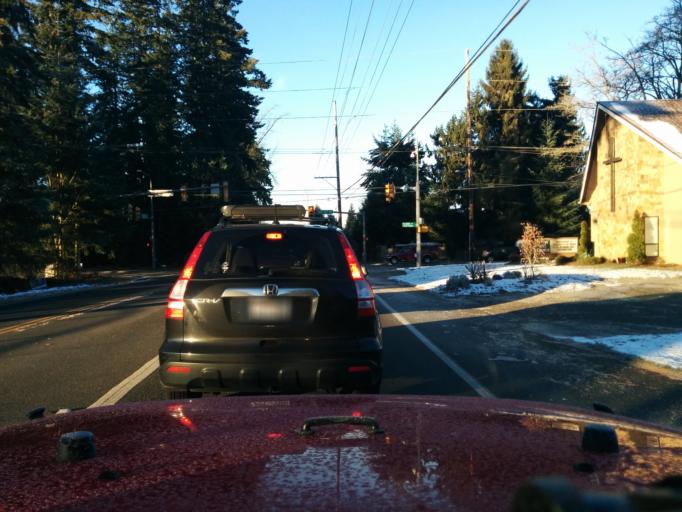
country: US
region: Washington
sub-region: King County
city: Union Hill-Novelty Hill
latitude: 47.6714
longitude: -122.0621
